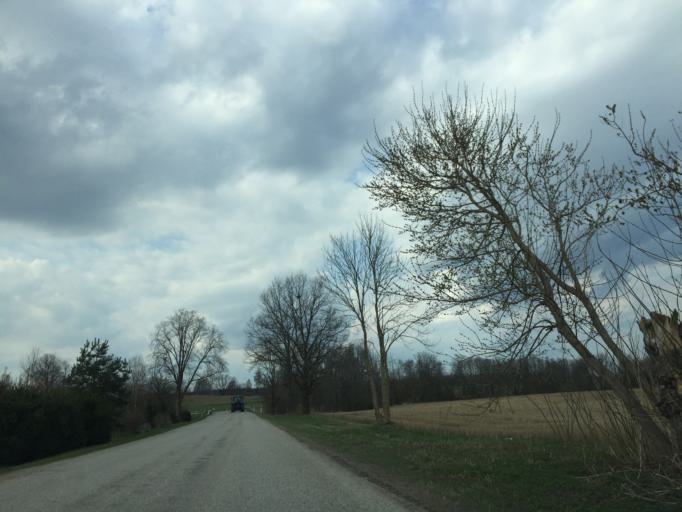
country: RU
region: Pskov
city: Pechory
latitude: 57.7308
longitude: 27.3516
